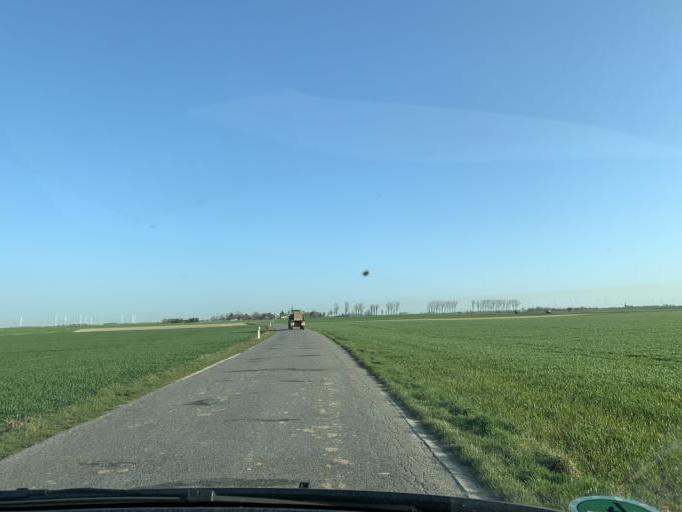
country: DE
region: North Rhine-Westphalia
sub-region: Regierungsbezirk Koln
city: Titz
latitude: 50.9769
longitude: 6.4642
